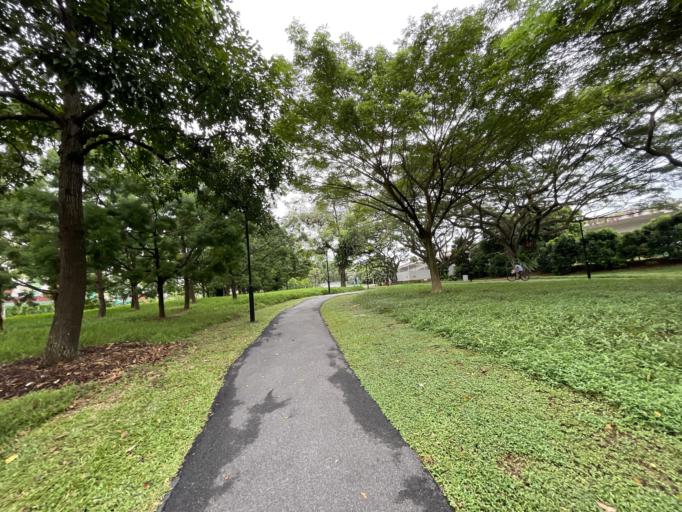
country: SG
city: Singapore
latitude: 1.2904
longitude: 103.7679
